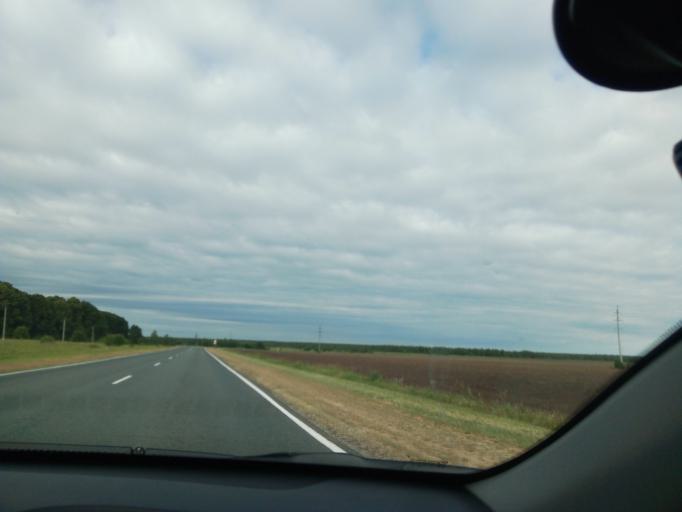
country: RU
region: Rjazan
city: Shatsk
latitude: 54.1426
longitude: 41.7459
